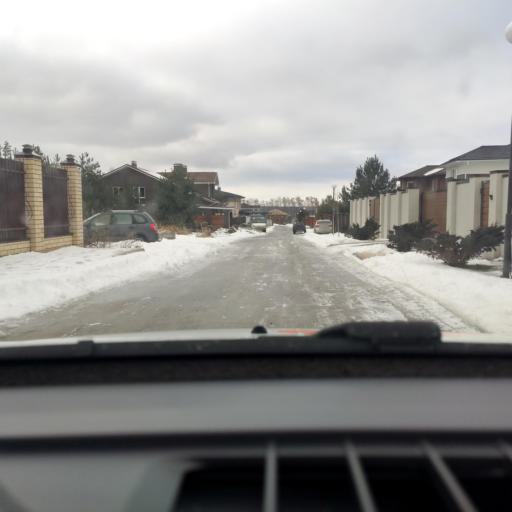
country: RU
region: Voronezj
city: Podgornoye
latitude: 51.7540
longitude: 39.1428
